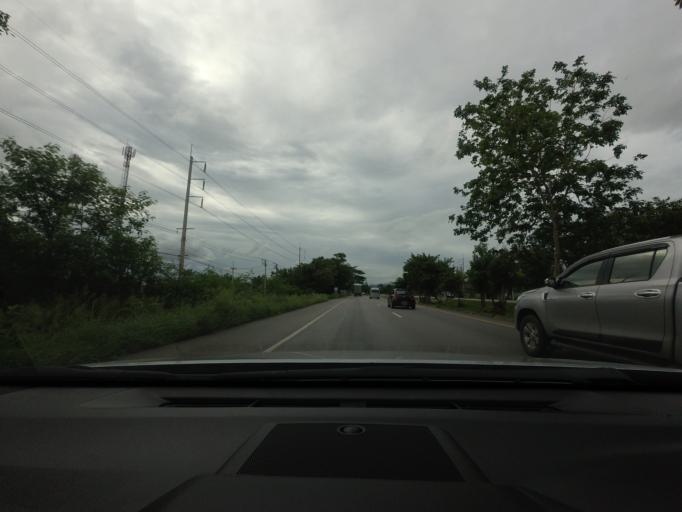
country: TH
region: Prachuap Khiri Khan
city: Hua Hin
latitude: 12.6219
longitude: 99.8586
